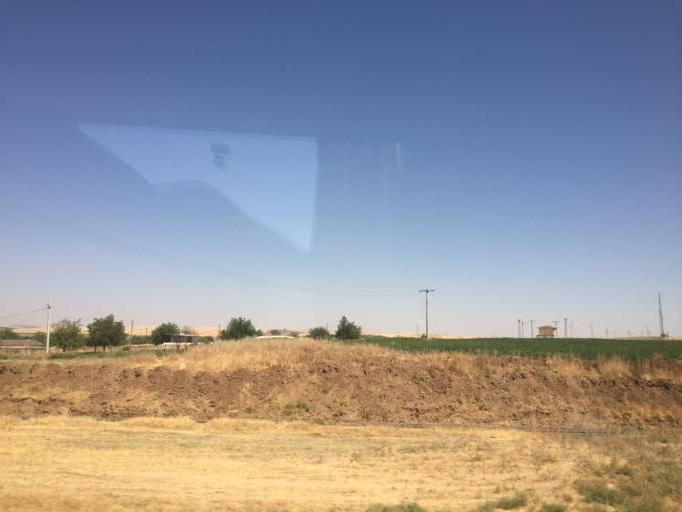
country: TR
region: Diyarbakir
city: Tepe
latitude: 37.8474
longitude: 40.8073
